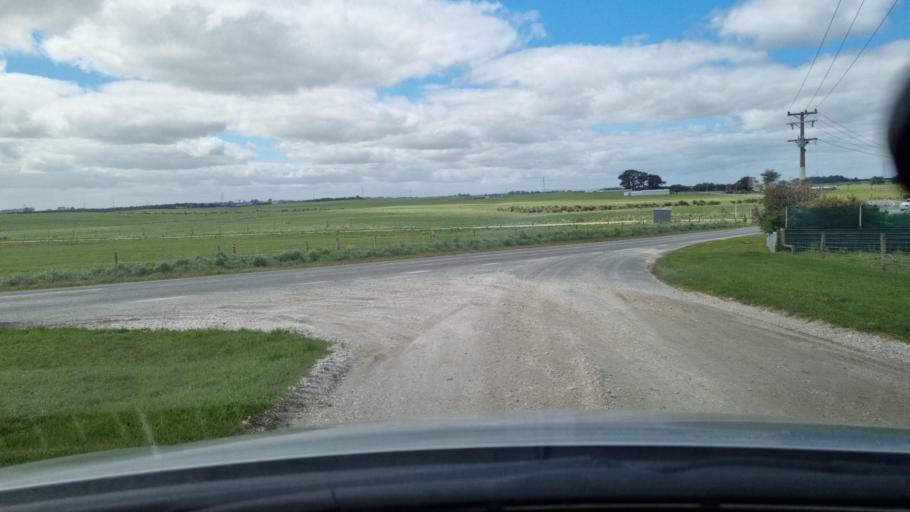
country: NZ
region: Southland
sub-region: Invercargill City
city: Invercargill
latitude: -46.4506
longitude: 168.4190
